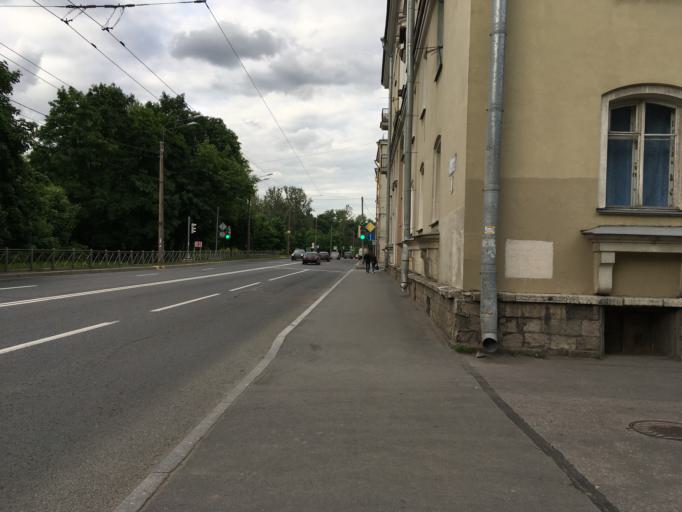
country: RU
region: St.-Petersburg
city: Centralniy
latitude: 59.8989
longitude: 30.3596
